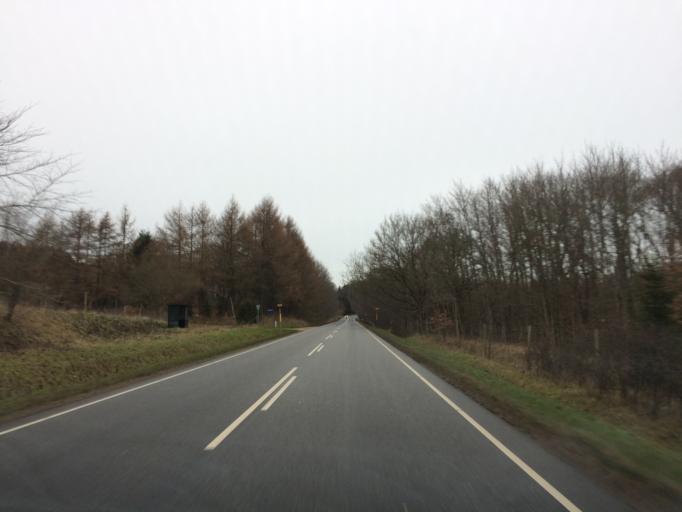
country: DK
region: Zealand
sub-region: Holbaek Kommune
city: Jyderup
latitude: 55.6266
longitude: 11.3951
